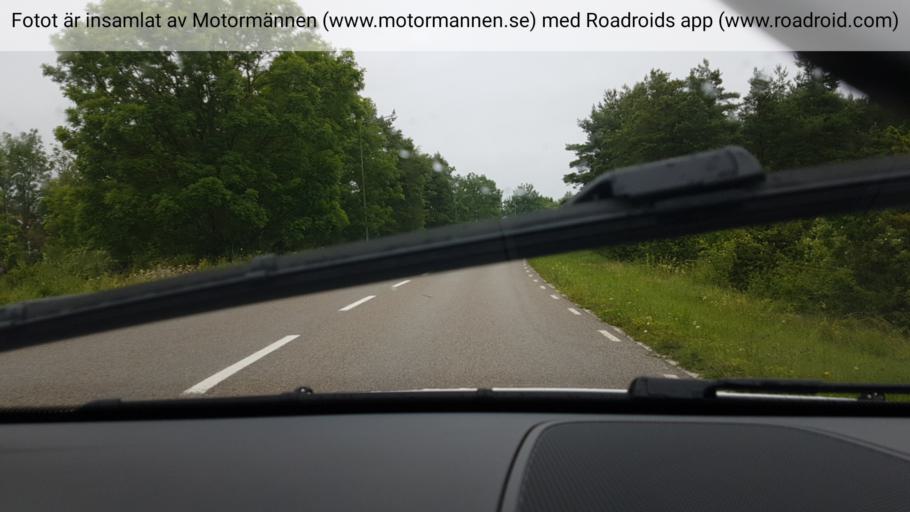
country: SE
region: Gotland
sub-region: Gotland
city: Slite
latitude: 57.8462
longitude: 18.7796
